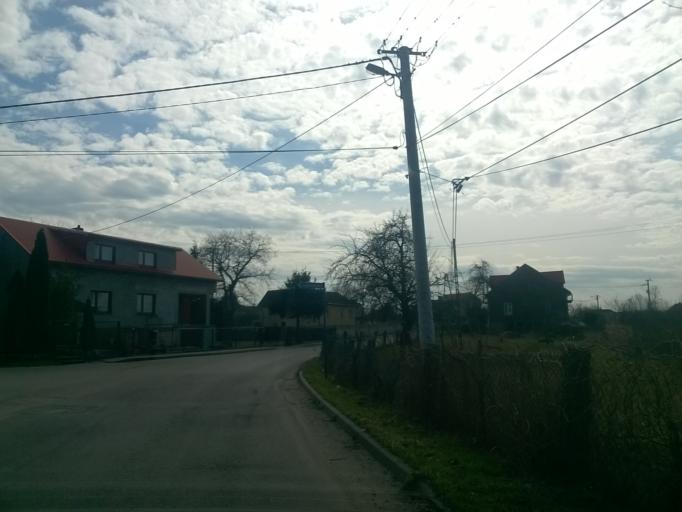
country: PL
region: Lesser Poland Voivodeship
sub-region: Powiat chrzanowski
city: Luszowice
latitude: 50.1761
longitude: 19.3996
